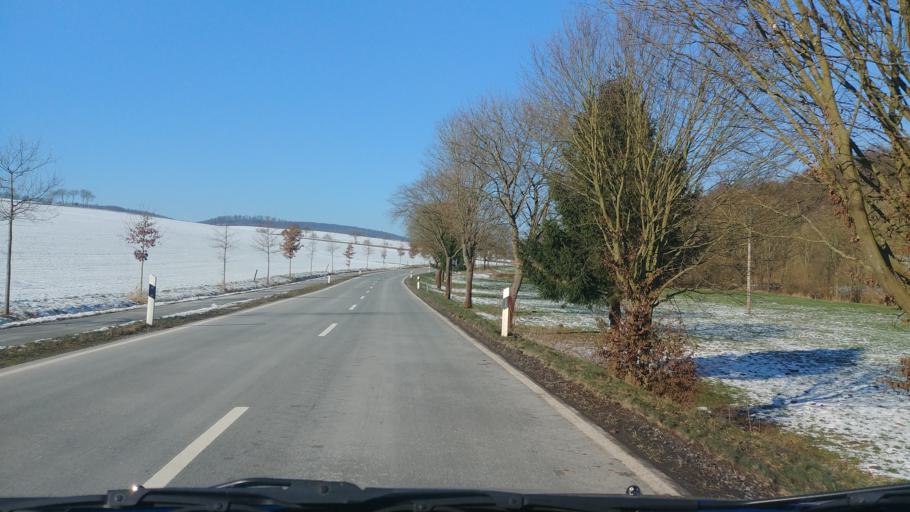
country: DE
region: Lower Saxony
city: Hardegsen
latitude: 51.6731
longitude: 9.7465
